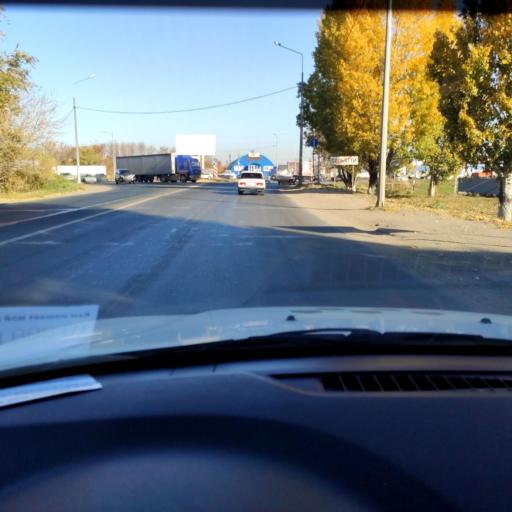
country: RU
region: Samara
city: Tol'yatti
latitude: 53.5714
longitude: 49.4600
